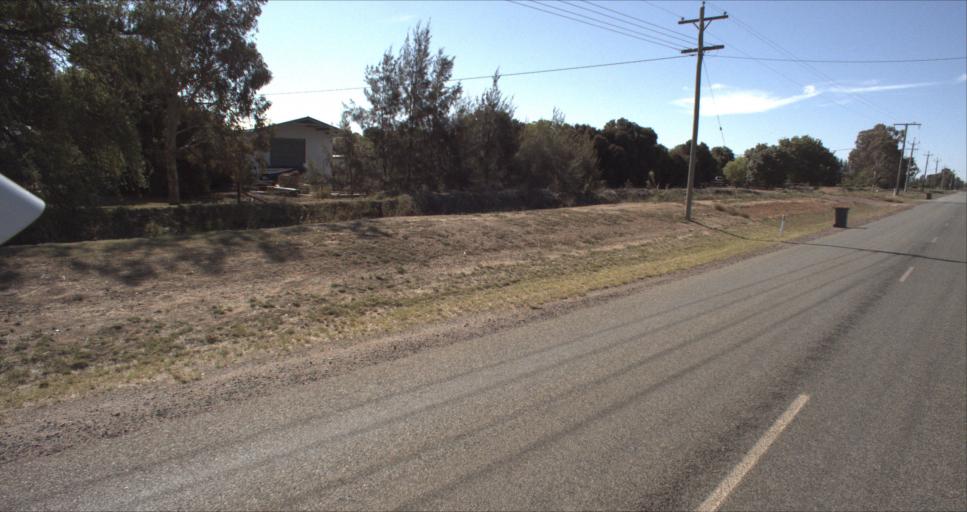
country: AU
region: New South Wales
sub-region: Leeton
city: Leeton
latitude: -34.5646
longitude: 146.3829
